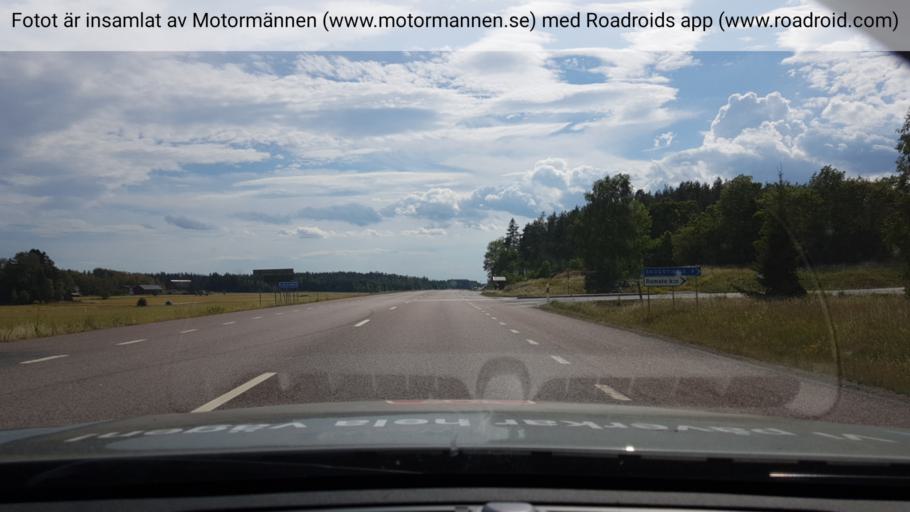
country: SE
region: Uppsala
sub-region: Enkopings Kommun
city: Orsundsbro
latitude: 59.7933
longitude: 17.4395
